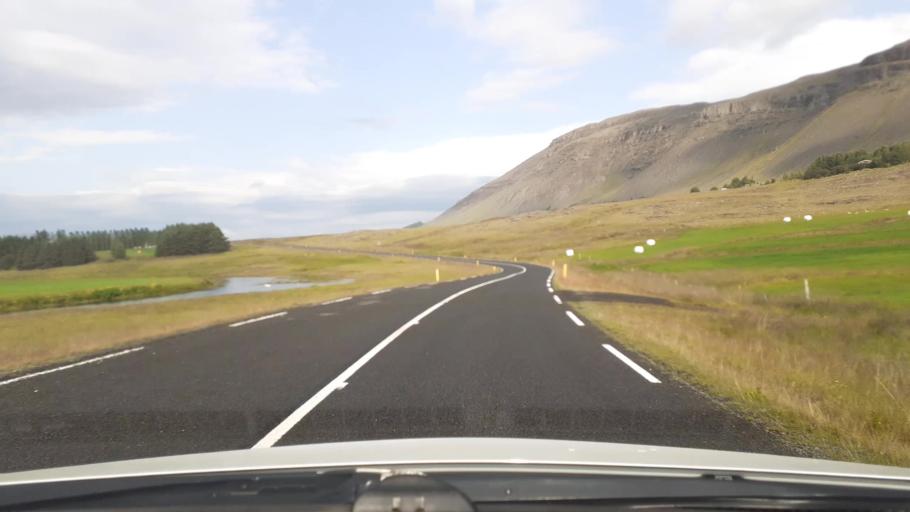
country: IS
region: Capital Region
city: Mosfellsbaer
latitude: 64.3414
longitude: -21.5819
